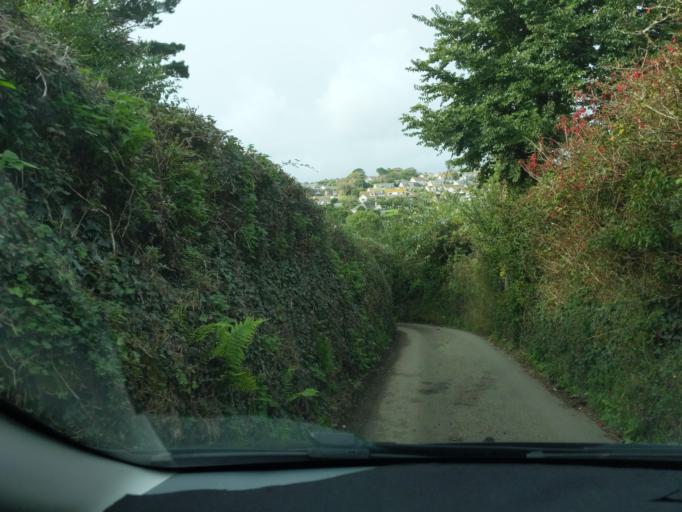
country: GB
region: England
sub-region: Cornwall
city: Mevagissey
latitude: 50.2389
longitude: -4.7906
